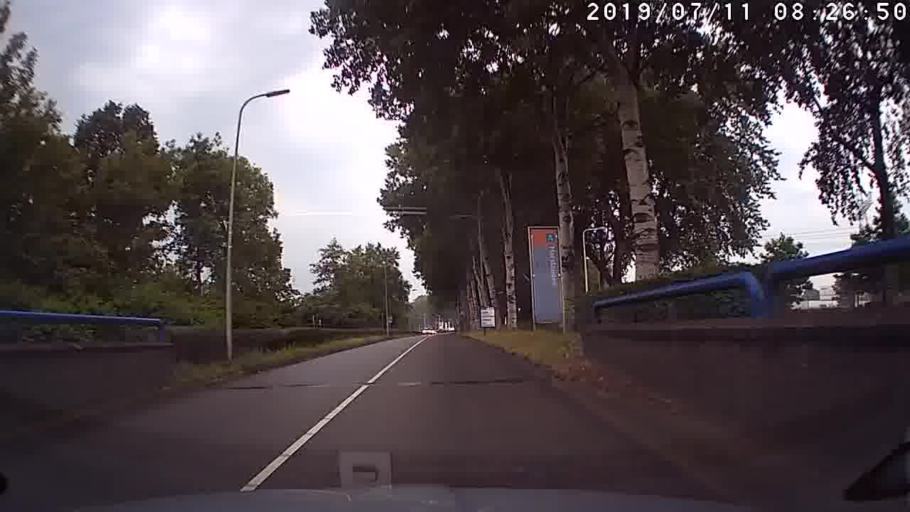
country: NL
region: Overijssel
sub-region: Gemeente Zwolle
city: Zwolle
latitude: 52.4994
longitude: 6.1223
